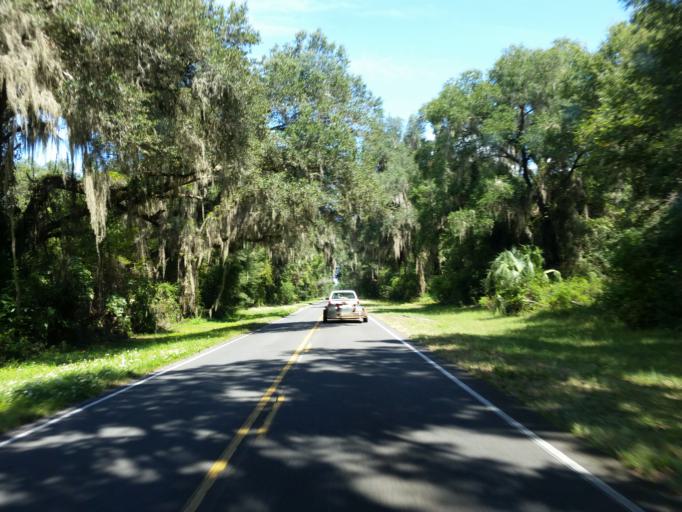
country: US
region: Florida
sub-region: Alachua County
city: Gainesville
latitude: 29.5713
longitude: -82.2551
